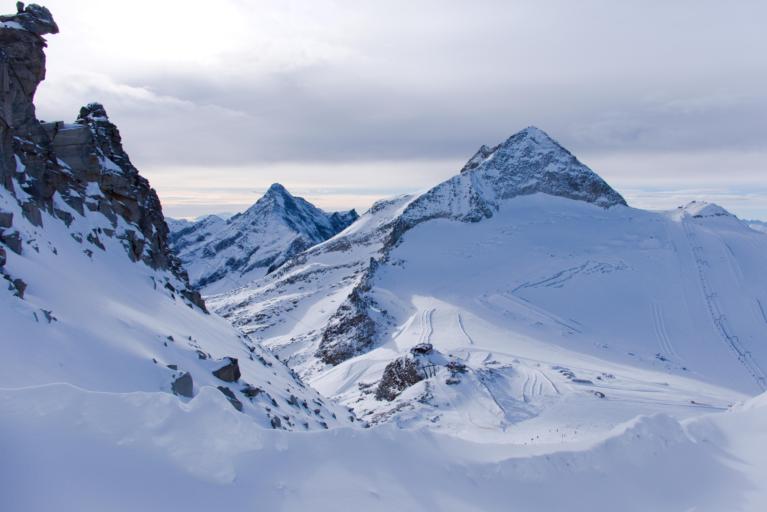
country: AT
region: Tyrol
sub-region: Politischer Bezirk Innsbruck Land
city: Schmirn
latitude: 47.0613
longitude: 11.6797
